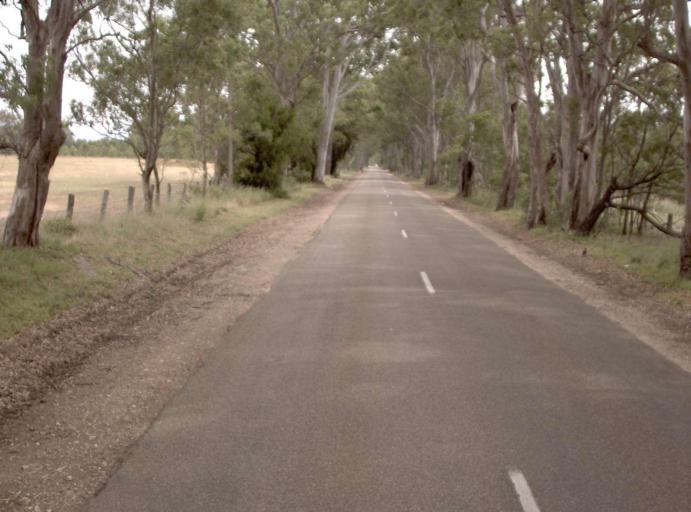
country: AU
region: Victoria
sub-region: Wellington
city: Sale
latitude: -37.8650
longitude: 147.0684
